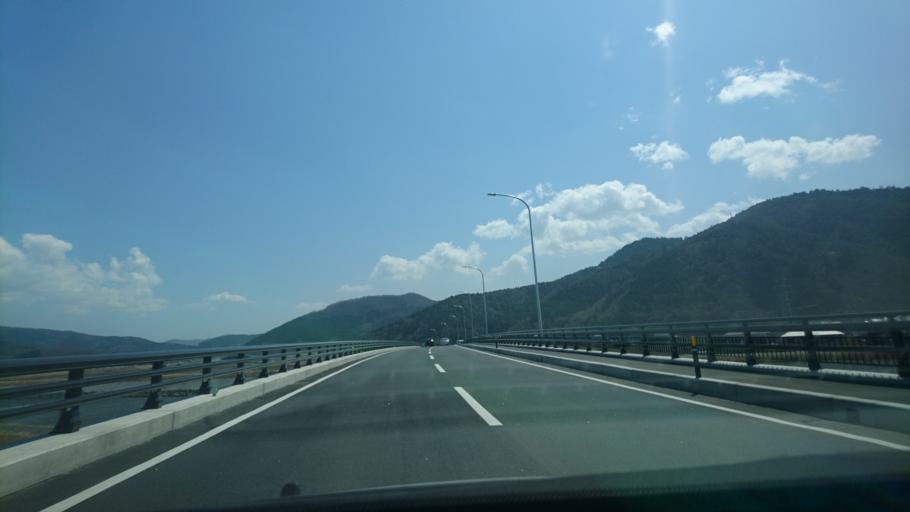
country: JP
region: Miyagi
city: Ishinomaki
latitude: 38.4515
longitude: 141.3367
